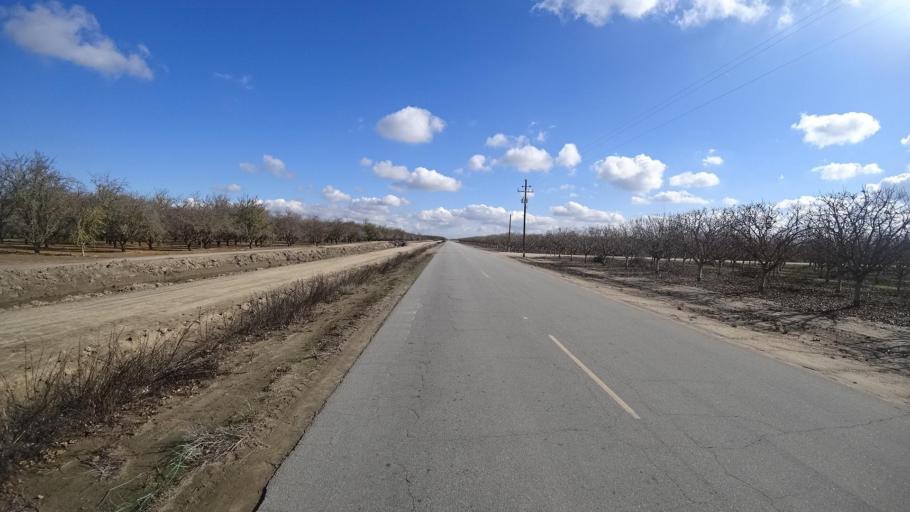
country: US
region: California
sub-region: Kern County
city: Wasco
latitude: 35.6742
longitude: -119.3174
